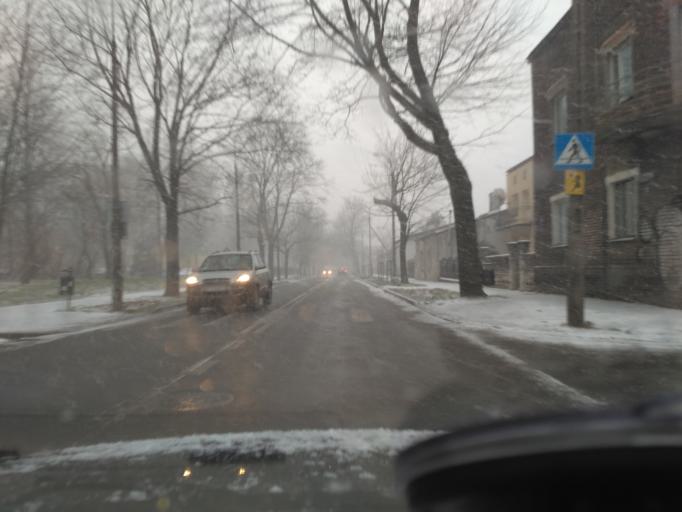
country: PL
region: Lublin Voivodeship
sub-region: Powiat lubelski
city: Lublin
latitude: 51.2316
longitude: 22.5849
